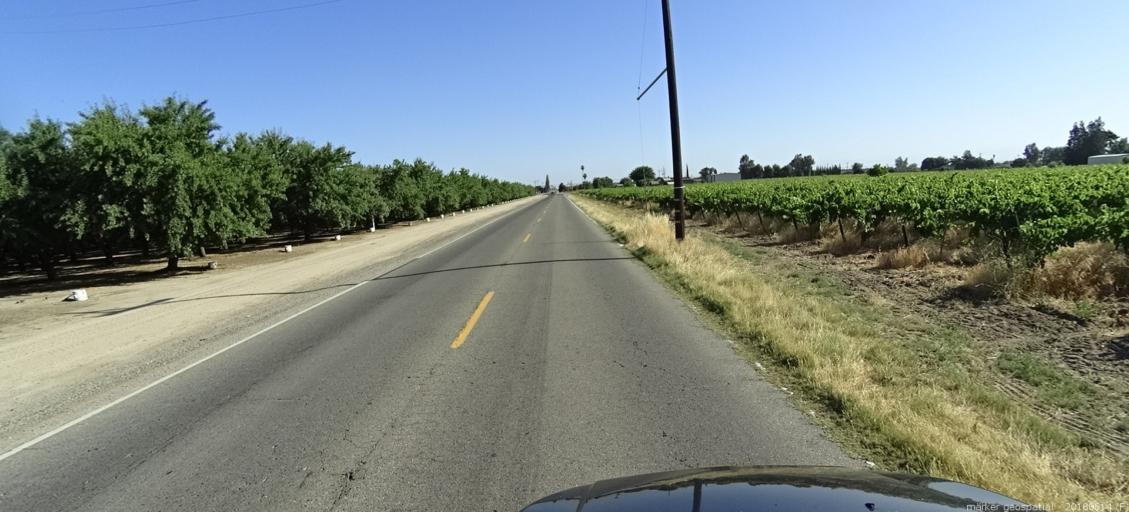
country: US
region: California
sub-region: Madera County
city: Madera
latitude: 36.9496
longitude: -120.1283
